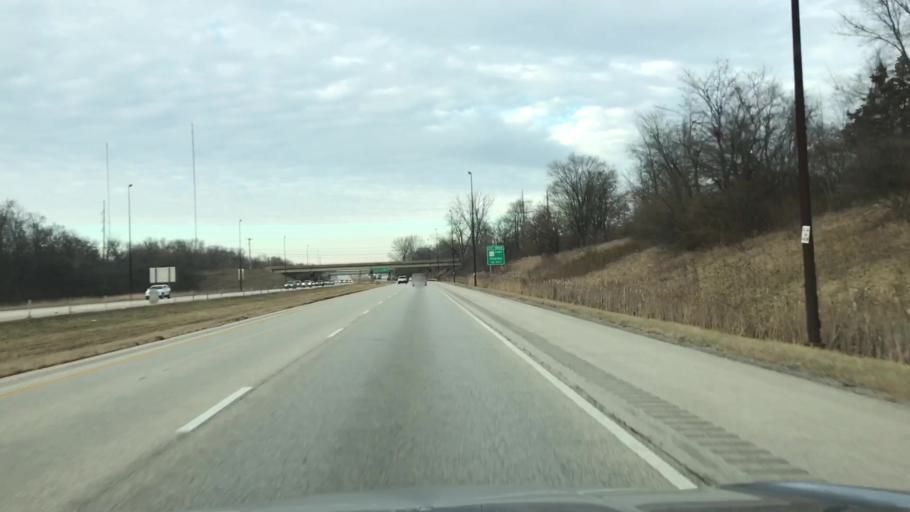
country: US
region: Illinois
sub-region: Sangamon County
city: Grandview
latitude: 39.8214
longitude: -89.5925
